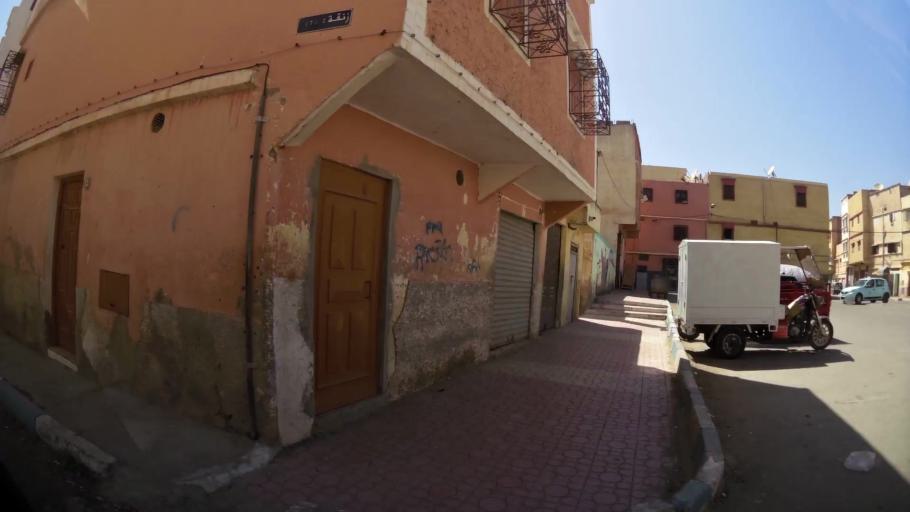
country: MA
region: Souss-Massa-Draa
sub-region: Inezgane-Ait Mellou
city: Inezgane
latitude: 30.3483
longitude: -9.5343
